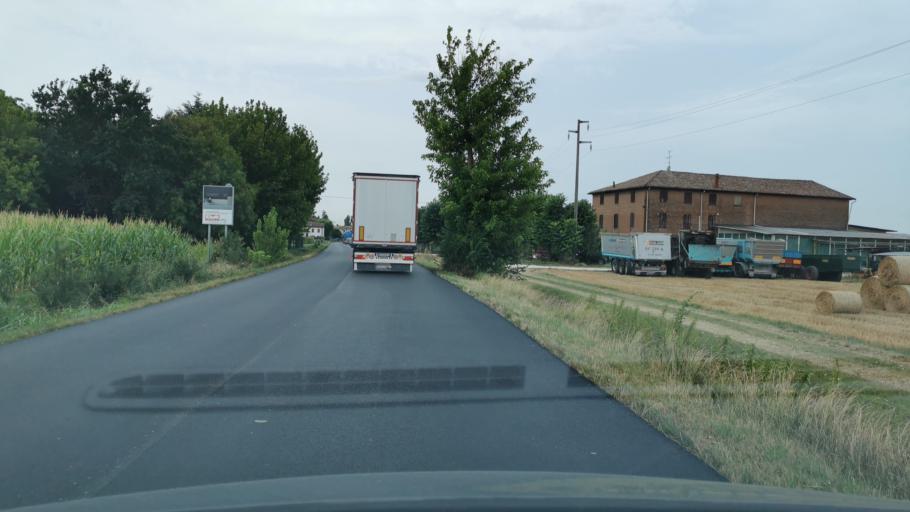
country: IT
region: Emilia-Romagna
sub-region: Provincia di Modena
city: Villanova
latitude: 44.7015
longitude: 10.8943
